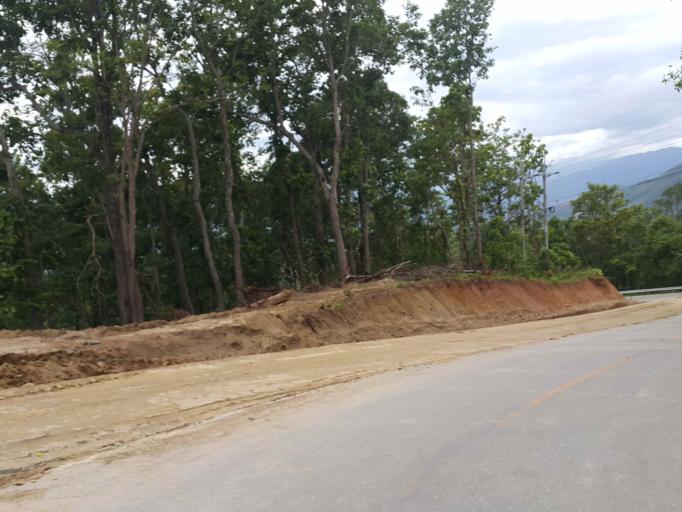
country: TH
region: Chiang Mai
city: Mae Chaem
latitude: 18.5090
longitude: 98.4356
